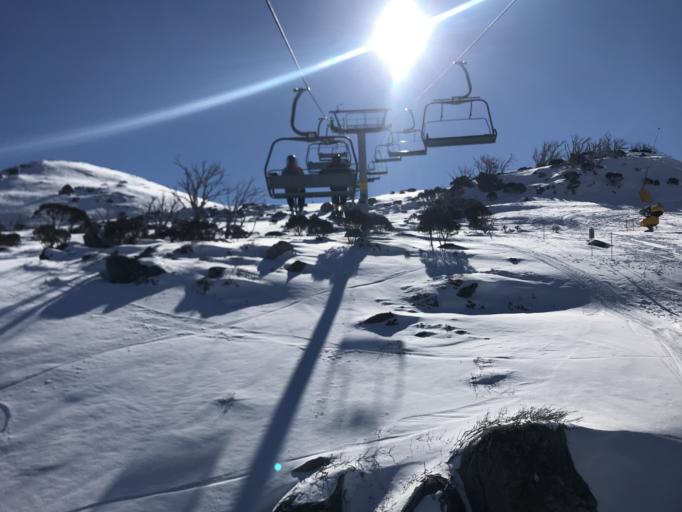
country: AU
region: New South Wales
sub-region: Snowy River
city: Jindabyne
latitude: -36.3807
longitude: 148.3969
